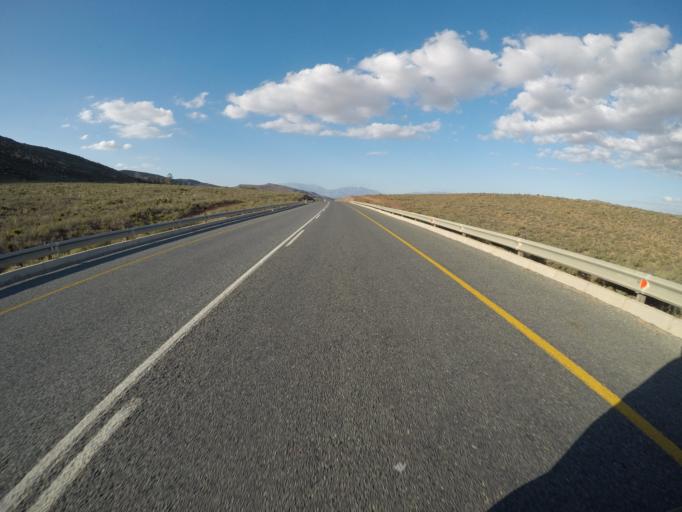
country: ZA
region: Western Cape
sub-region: Cape Winelands District Municipality
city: Worcester
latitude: -33.8103
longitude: 19.4320
